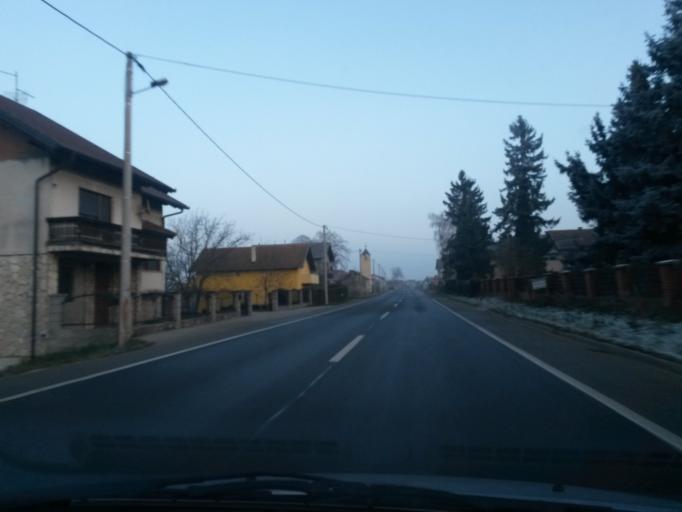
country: HR
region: Varazdinska
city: Ludbreg
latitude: 46.2321
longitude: 16.6575
